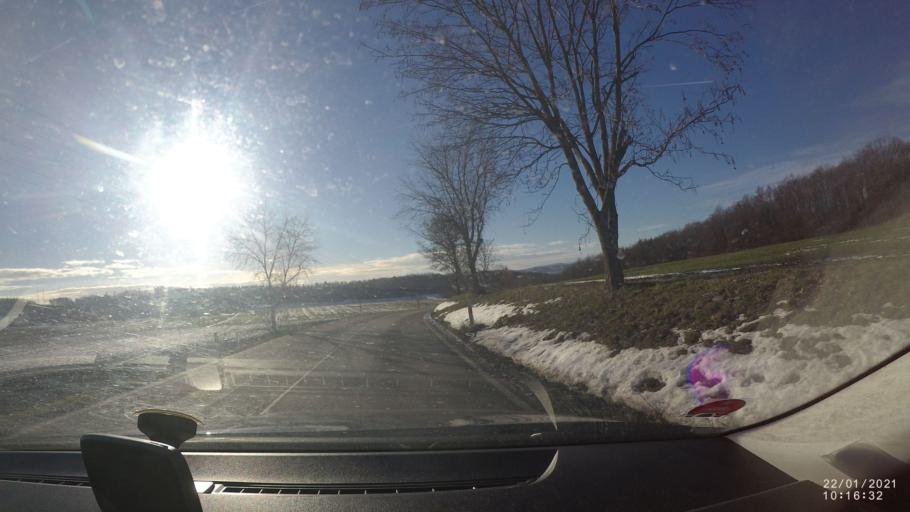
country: CZ
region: Central Bohemia
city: Chynava
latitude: 50.0006
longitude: 14.0936
